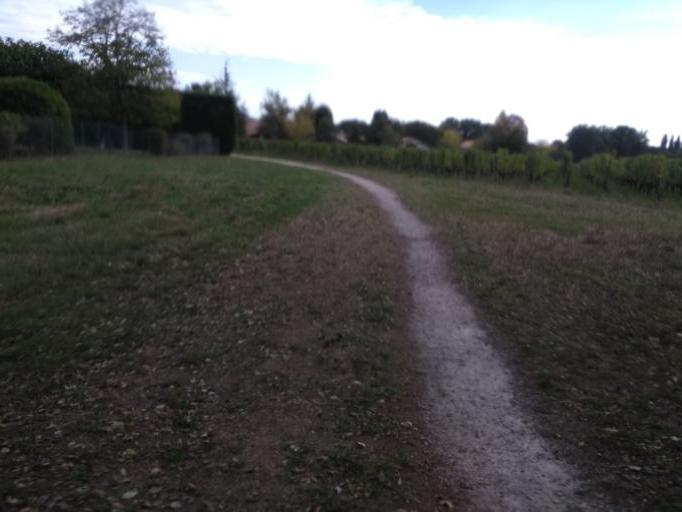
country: FR
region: Aquitaine
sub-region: Departement de la Gironde
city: Canejan
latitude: 44.7707
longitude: -0.6371
